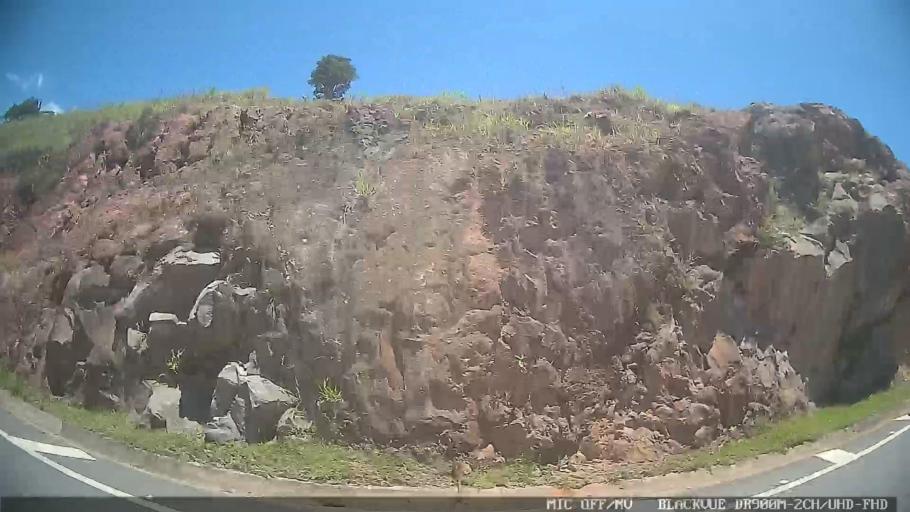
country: BR
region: Sao Paulo
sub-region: Santa Branca
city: Santa Branca
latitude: -23.3725
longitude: -45.6675
